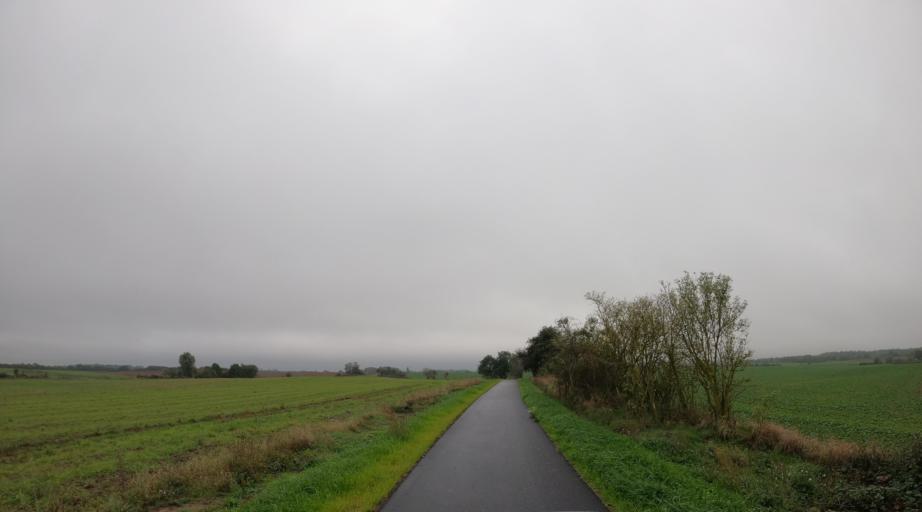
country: PL
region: West Pomeranian Voivodeship
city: Trzcinsko Zdroj
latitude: 52.9280
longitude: 14.7293
